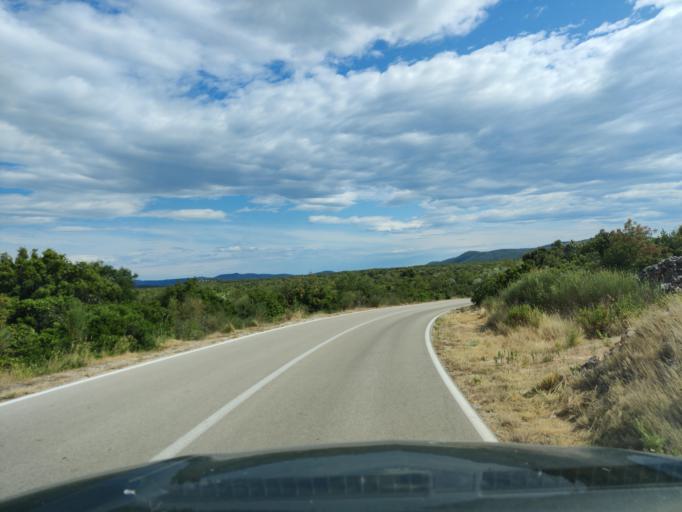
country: HR
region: Sibensko-Kniniska
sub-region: Grad Sibenik
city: Sibenik
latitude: 43.7399
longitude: 15.8592
